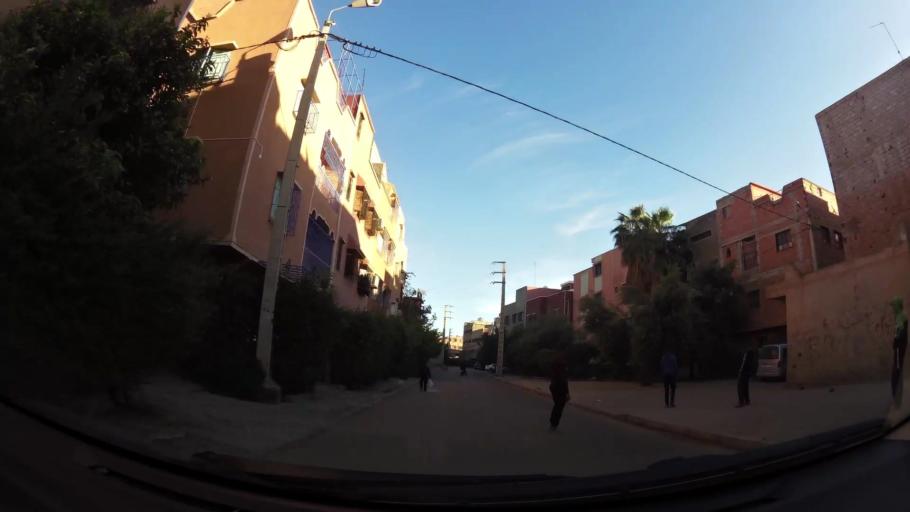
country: MA
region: Marrakech-Tensift-Al Haouz
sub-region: Marrakech
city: Marrakesh
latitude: 31.6214
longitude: -8.0559
